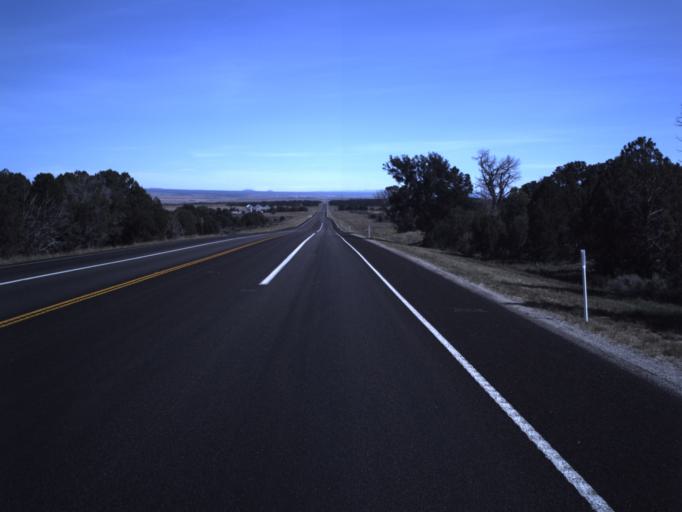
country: US
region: Colorado
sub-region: Dolores County
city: Dove Creek
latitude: 37.8387
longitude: -109.1195
